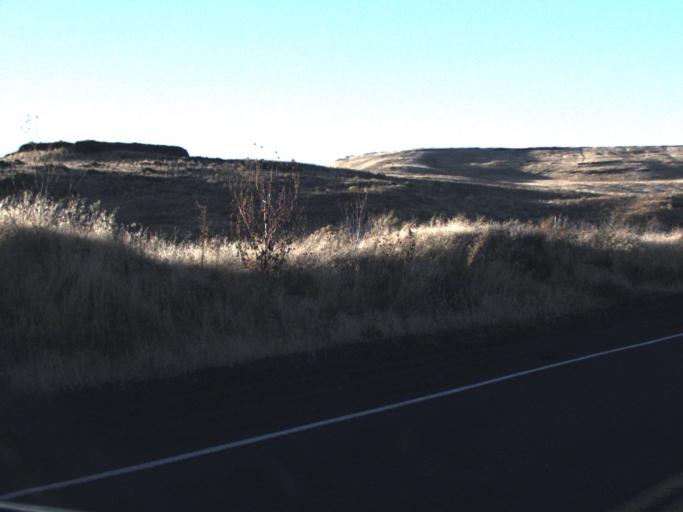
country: US
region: Washington
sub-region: Walla Walla County
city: Waitsburg
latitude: 46.5999
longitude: -118.2251
